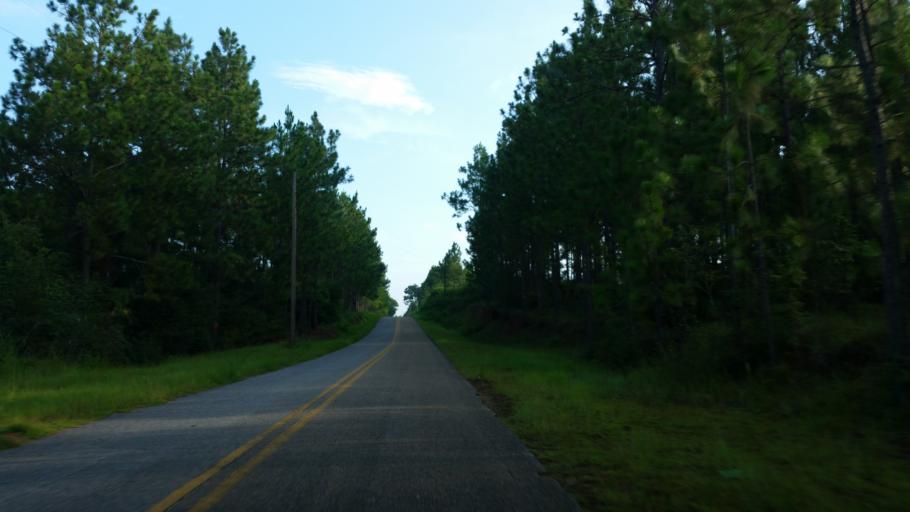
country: US
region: Alabama
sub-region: Escambia County
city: Atmore
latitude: 30.9756
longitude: -87.5712
